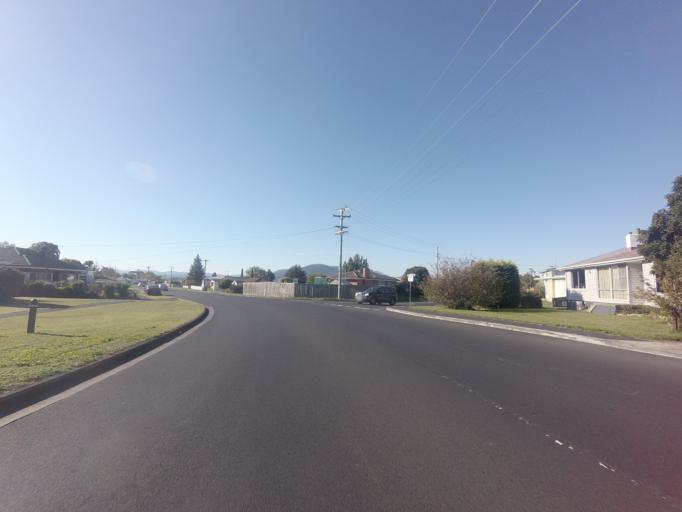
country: AU
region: Tasmania
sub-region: Glenorchy
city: Glenorchy
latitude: -42.8441
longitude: 147.2686
